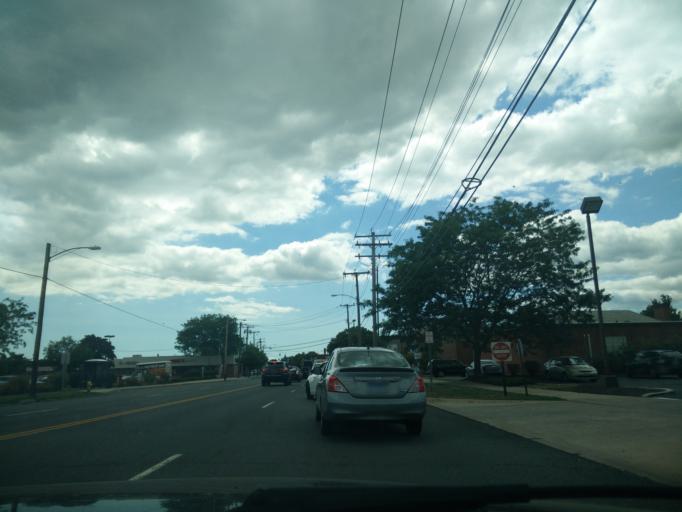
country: US
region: Connecticut
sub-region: New Haven County
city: New Haven
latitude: 41.3479
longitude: -72.9332
